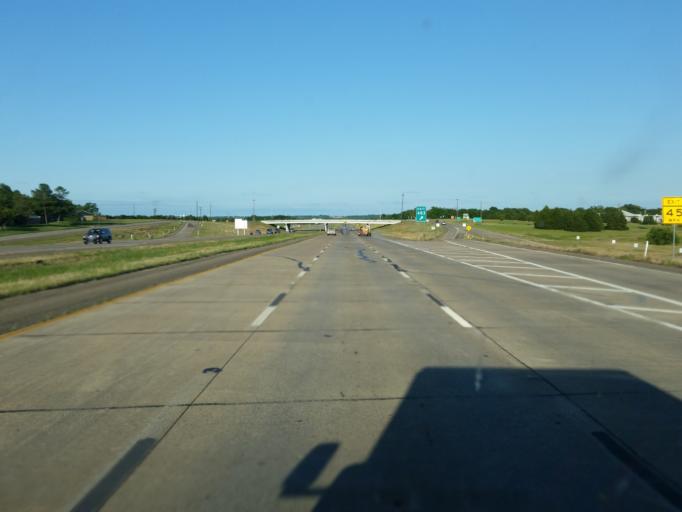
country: US
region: Texas
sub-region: Dallas County
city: Balch Springs
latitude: 32.7039
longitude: -96.5745
